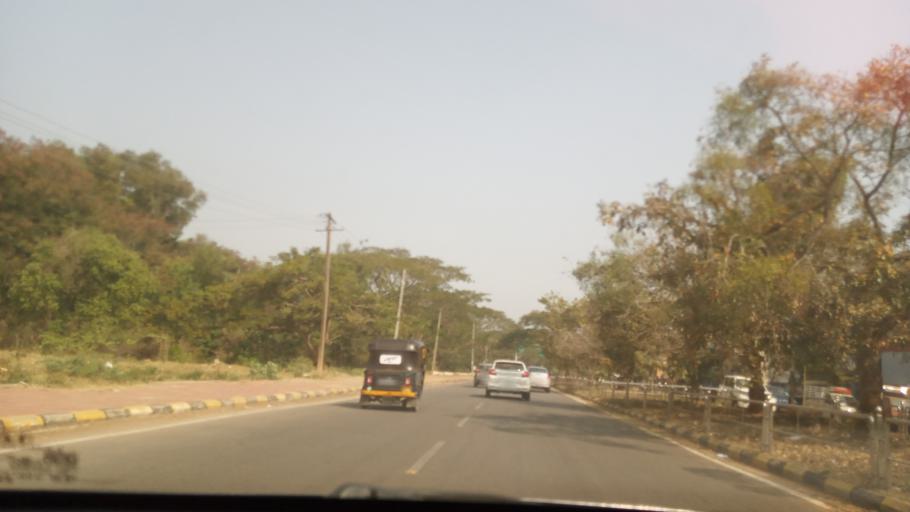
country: IN
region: Karnataka
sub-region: Mysore
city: Mysore
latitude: 12.3042
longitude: 76.6267
